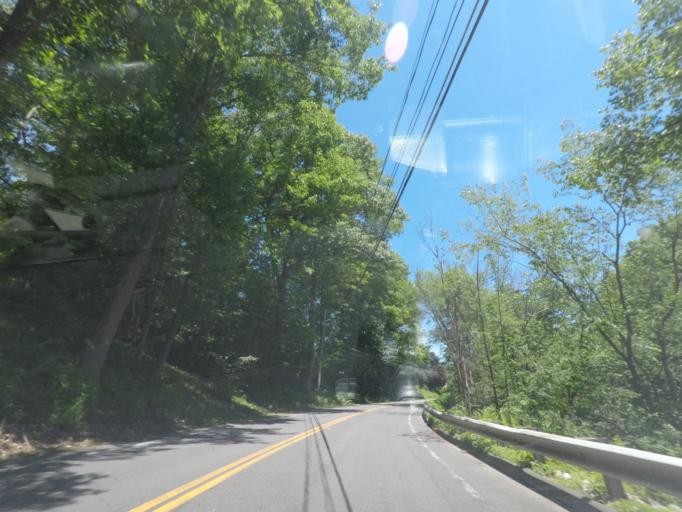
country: US
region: Massachusetts
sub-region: Berkshire County
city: Becket
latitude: 42.2802
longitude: -72.9874
